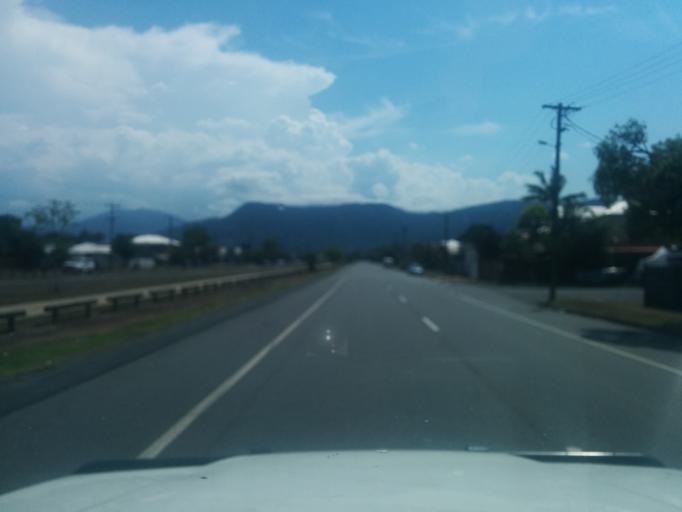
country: AU
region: Queensland
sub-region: Cairns
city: Cairns
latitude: -16.9361
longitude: 145.7612
